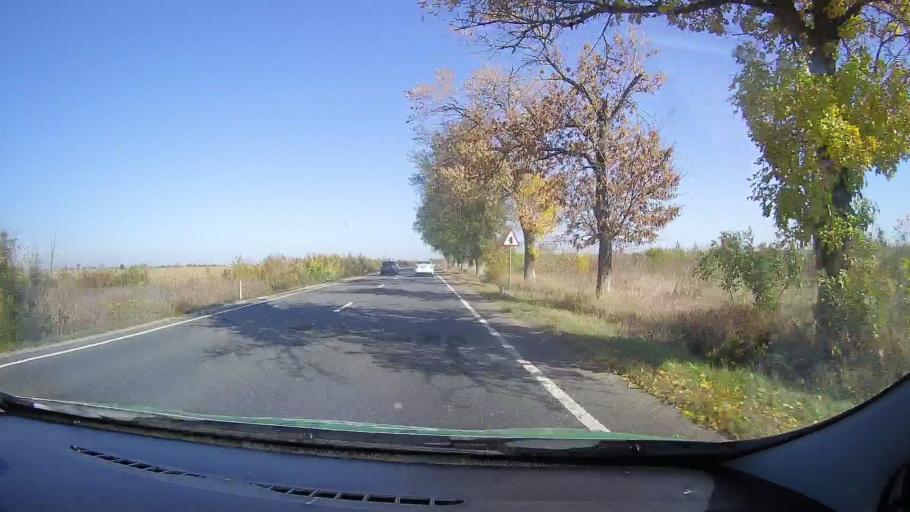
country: RO
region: Satu Mare
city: Moftinu Mare
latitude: 47.7129
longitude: 22.6461
